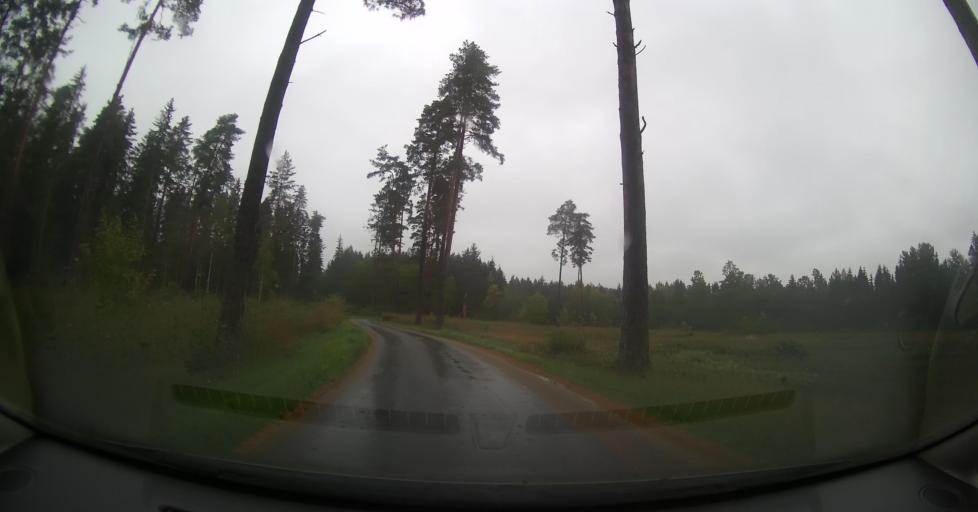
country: EE
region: Tartu
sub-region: UElenurme vald
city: Ulenurme
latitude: 58.3459
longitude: 26.8062
